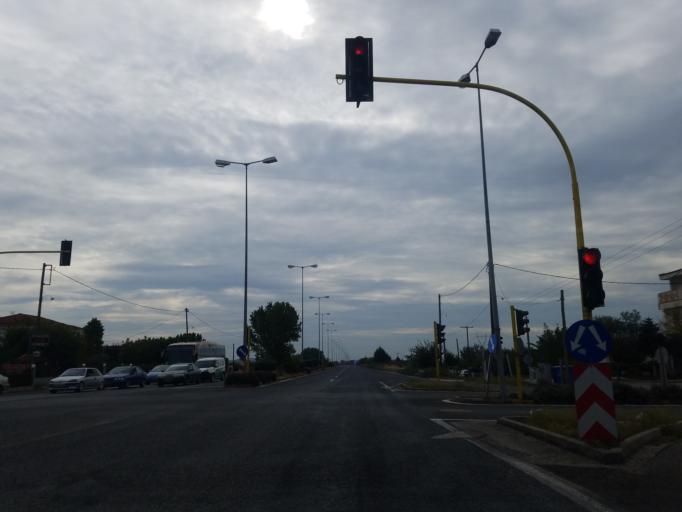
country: GR
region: Thessaly
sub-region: Trikala
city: Vasiliki
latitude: 39.6347
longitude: 21.6993
